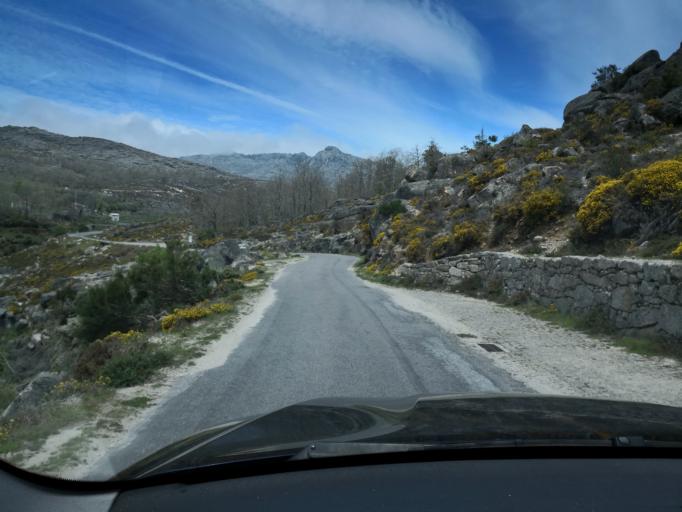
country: PT
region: Vila Real
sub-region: Vila Real
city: Vila Real
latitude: 41.3246
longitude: -7.7989
